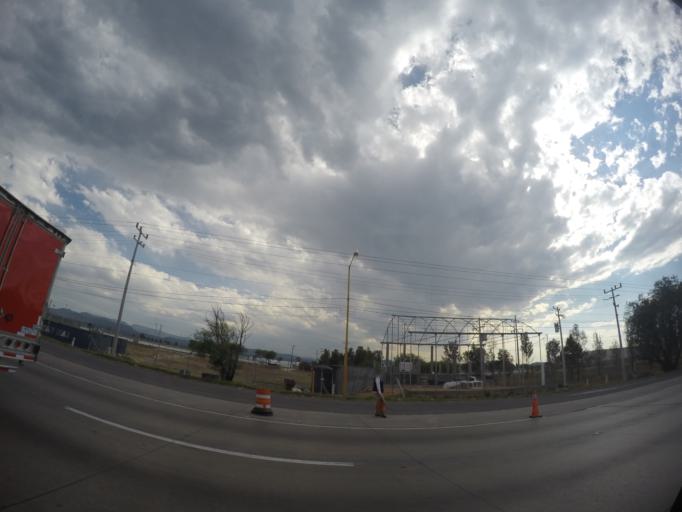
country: MX
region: Queretaro
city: La Estancia
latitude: 20.4304
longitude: -100.0606
